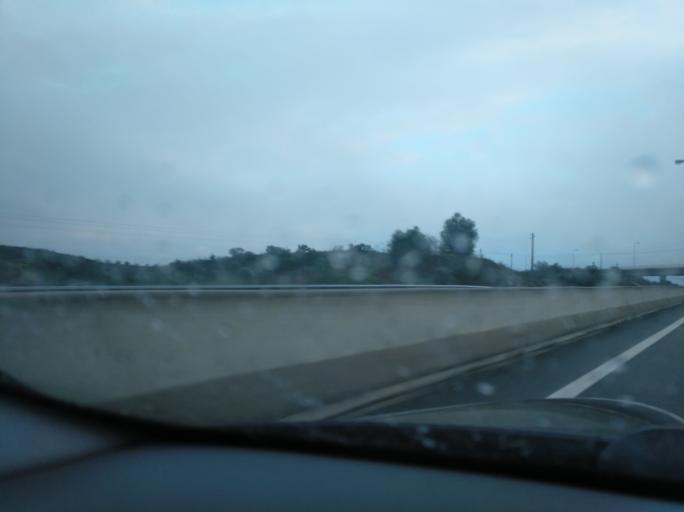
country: PT
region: Faro
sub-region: Castro Marim
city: Castro Marim
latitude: 37.2950
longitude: -7.4878
